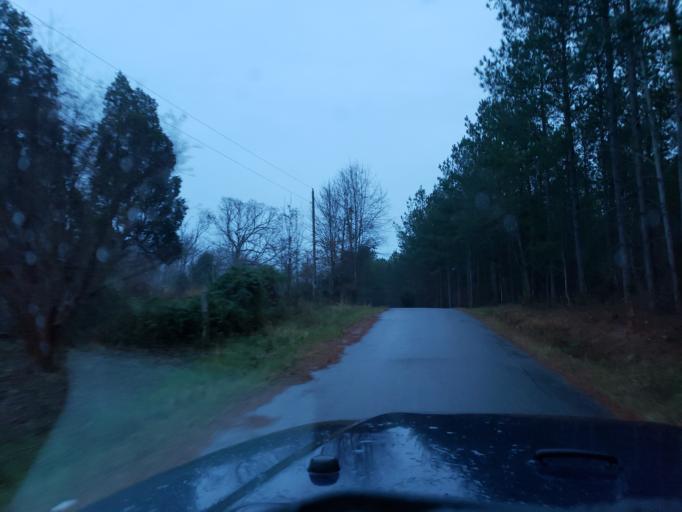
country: US
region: North Carolina
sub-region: Cleveland County
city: White Plains
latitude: 35.1486
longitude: -81.4241
